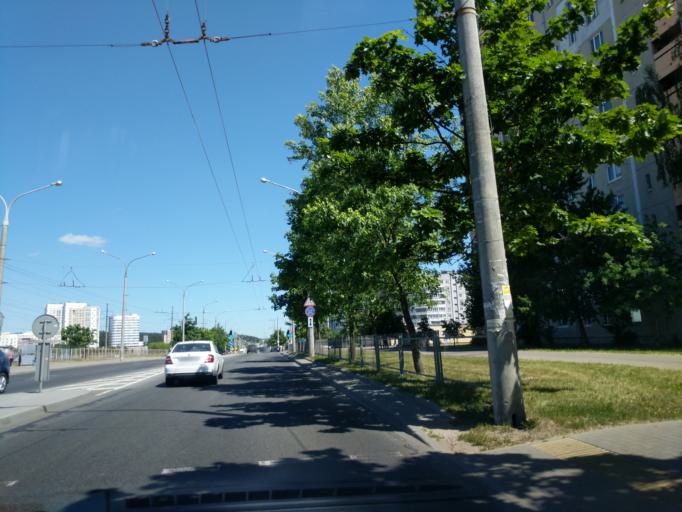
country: BY
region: Minsk
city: Borovlyany
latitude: 53.9487
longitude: 27.6695
